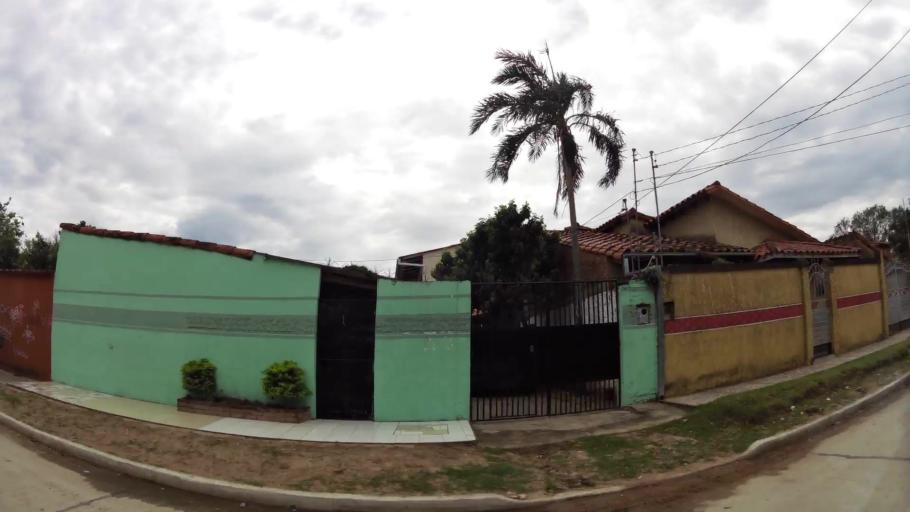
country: BO
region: Santa Cruz
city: Santa Cruz de la Sierra
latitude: -17.7372
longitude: -63.1928
